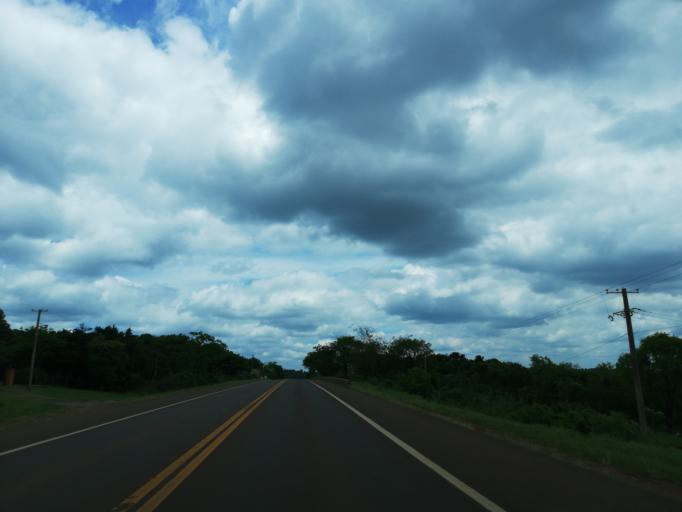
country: AR
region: Misiones
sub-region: Departamento de Leandro N. Alem
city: Leandro N. Alem
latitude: -27.6327
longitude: -55.3429
